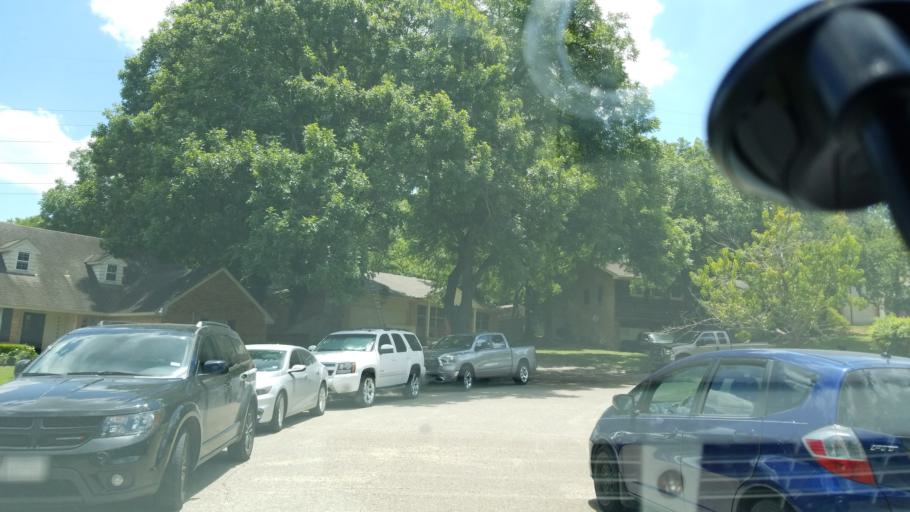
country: US
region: Texas
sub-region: Dallas County
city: Cockrell Hill
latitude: 32.7007
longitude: -96.8517
